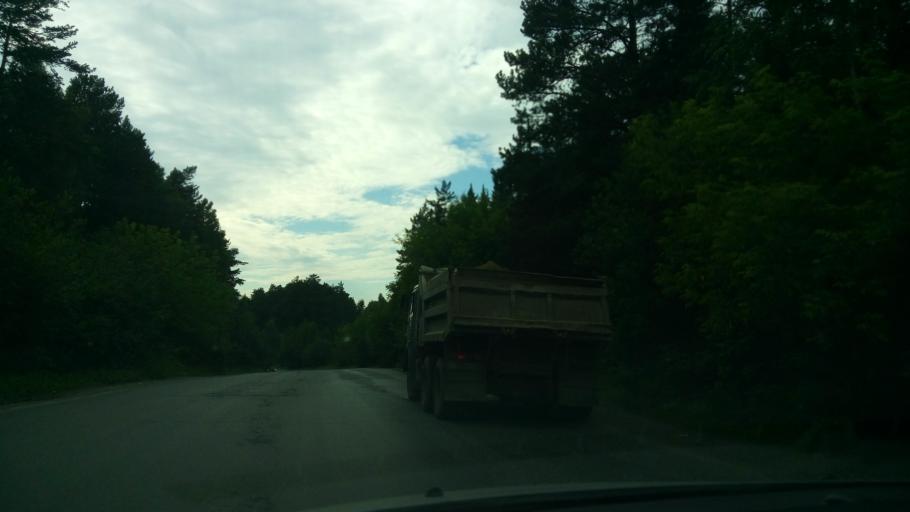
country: RU
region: Sverdlovsk
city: Yekaterinburg
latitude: 56.8867
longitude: 60.6751
